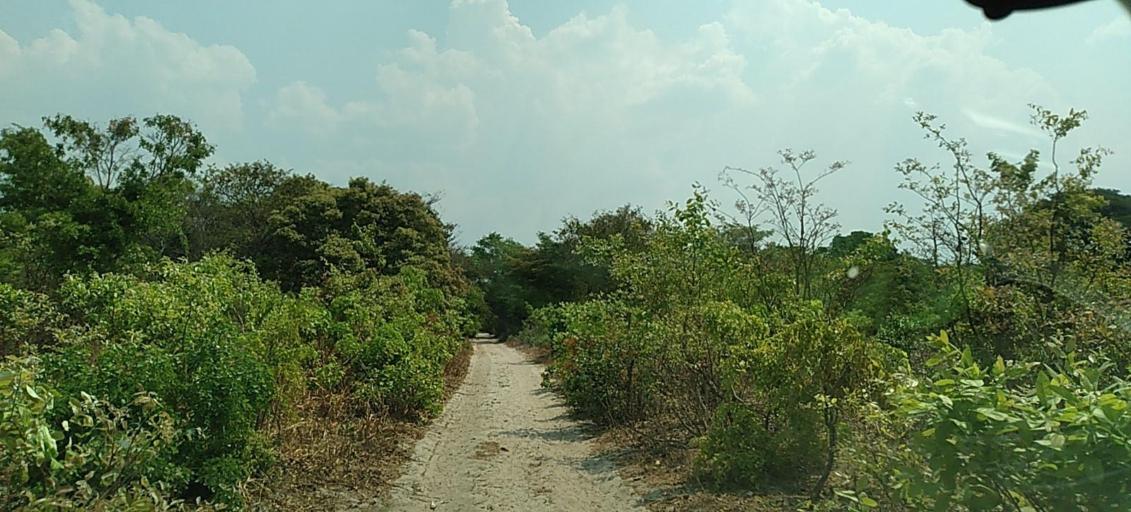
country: ZM
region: North-Western
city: Kabompo
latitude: -13.3866
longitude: 23.7663
